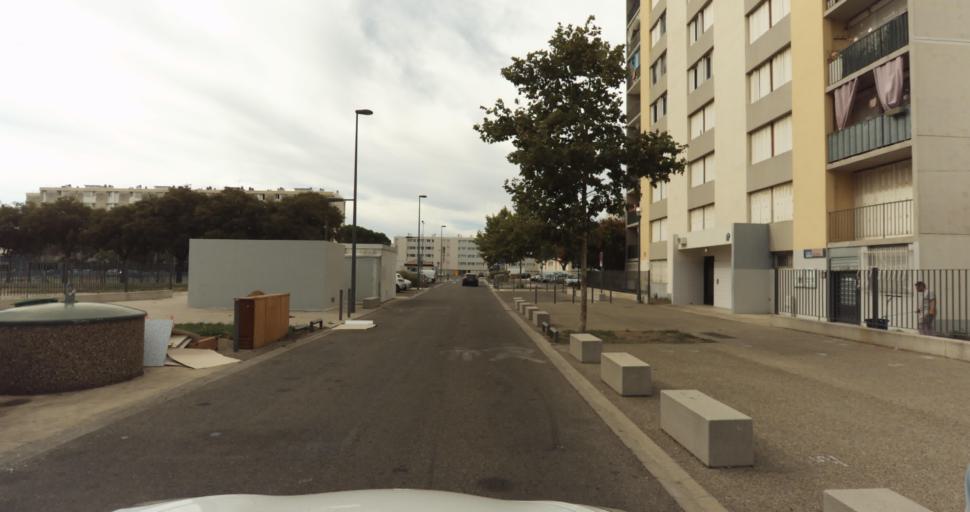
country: FR
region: Provence-Alpes-Cote d'Azur
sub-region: Departement des Bouches-du-Rhone
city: Miramas
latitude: 43.5921
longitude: 5.0065
